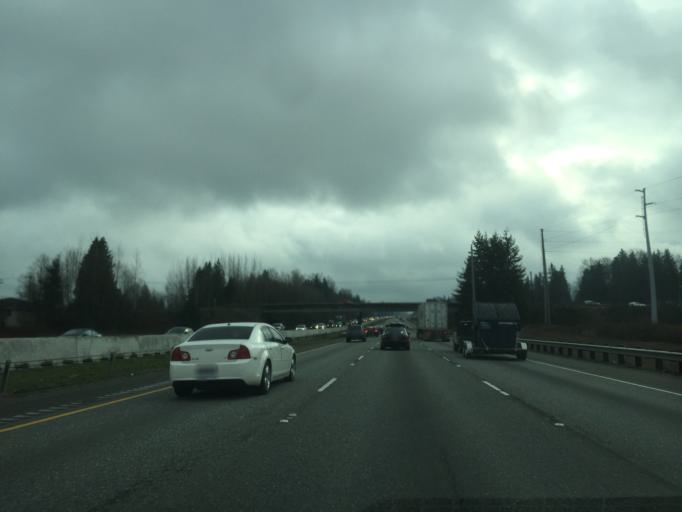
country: US
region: Washington
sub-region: Snohomish County
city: Smokey Point
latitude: 48.1202
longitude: -122.1854
